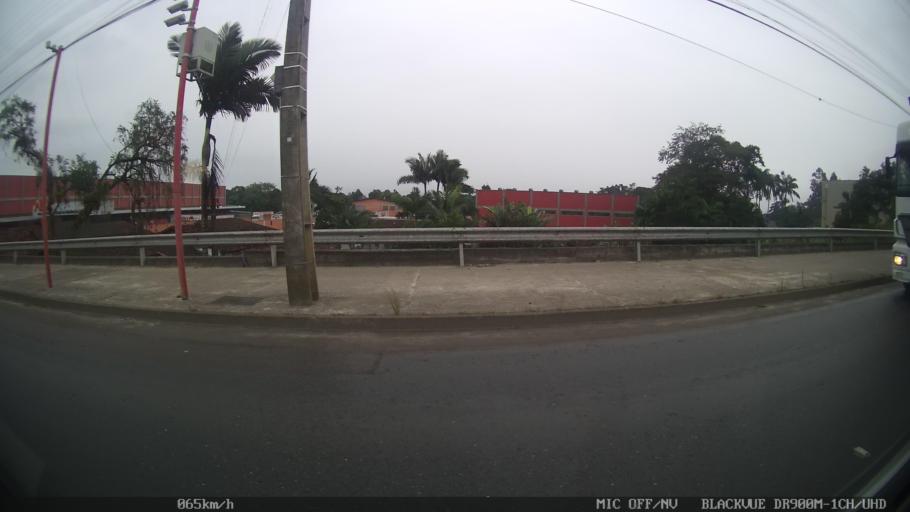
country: BR
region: Santa Catarina
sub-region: Joinville
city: Joinville
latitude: -26.2422
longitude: -48.8340
